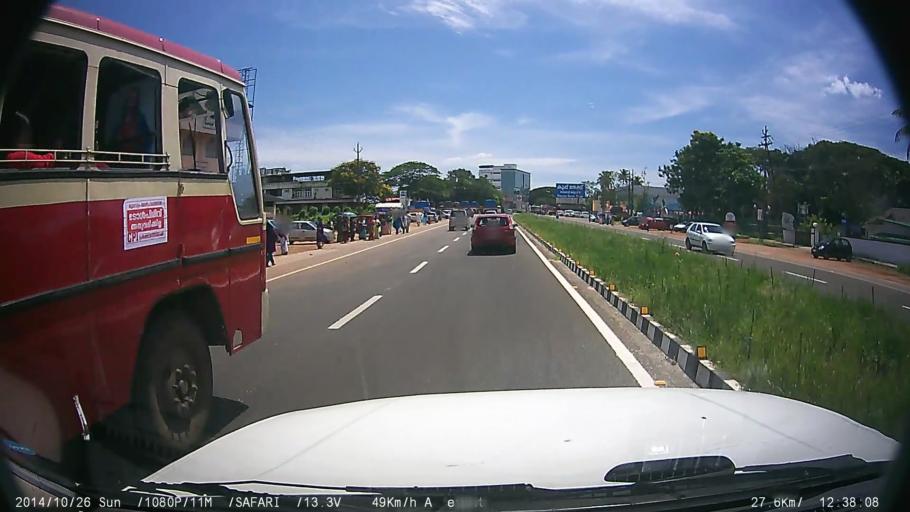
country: IN
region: Kerala
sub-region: Kottayam
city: Kottayam
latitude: 9.5705
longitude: 76.5198
